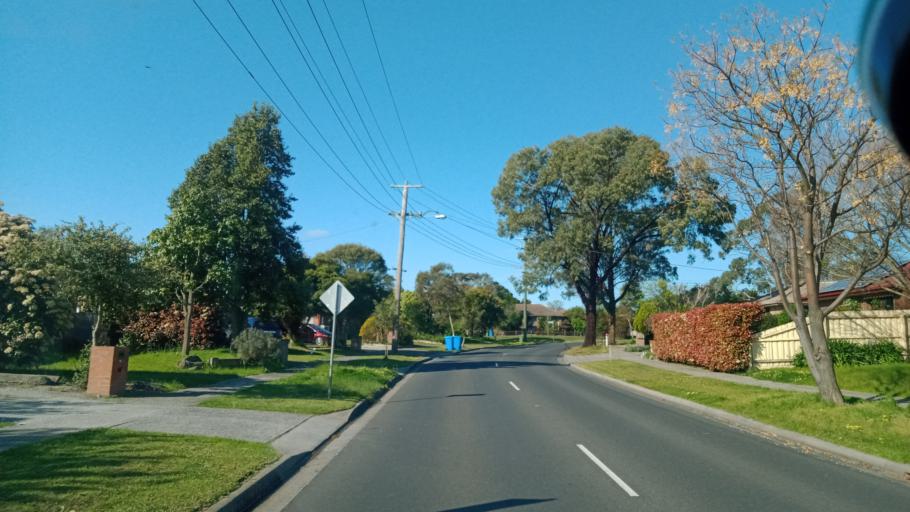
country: AU
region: Victoria
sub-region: Casey
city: Cranbourne West
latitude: -38.1016
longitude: 145.2703
